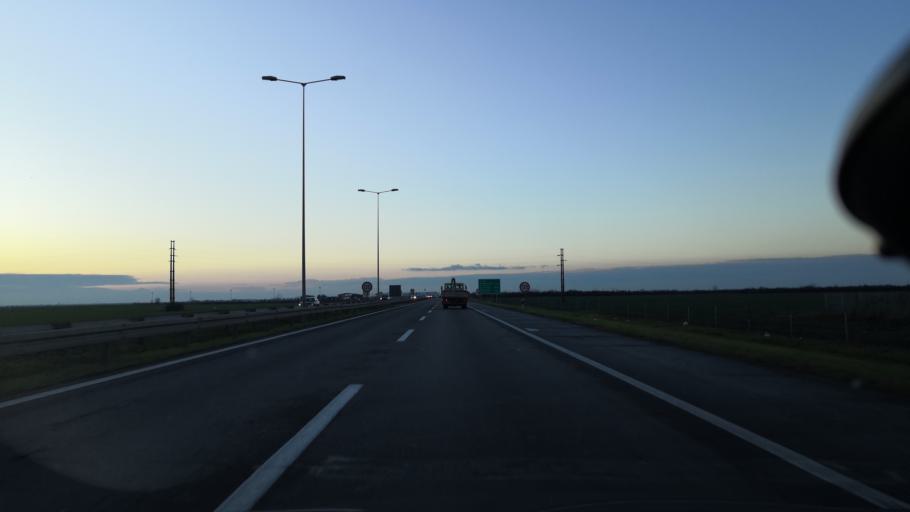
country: RS
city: Dobanovci
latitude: 44.8461
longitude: 20.2037
